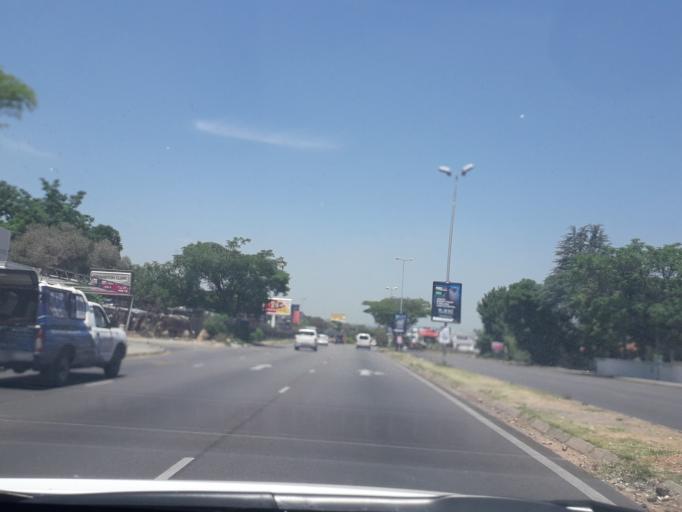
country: ZA
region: Gauteng
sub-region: City of Johannesburg Metropolitan Municipality
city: Diepsloot
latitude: -26.0548
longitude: 28.0219
